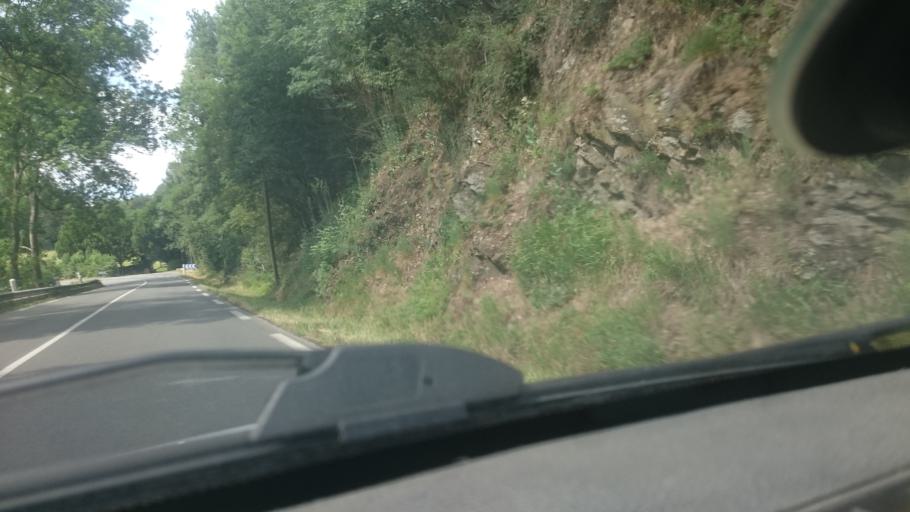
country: FR
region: Rhone-Alpes
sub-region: Departement du Rhone
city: Lozanne
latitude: 45.8578
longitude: 4.6593
